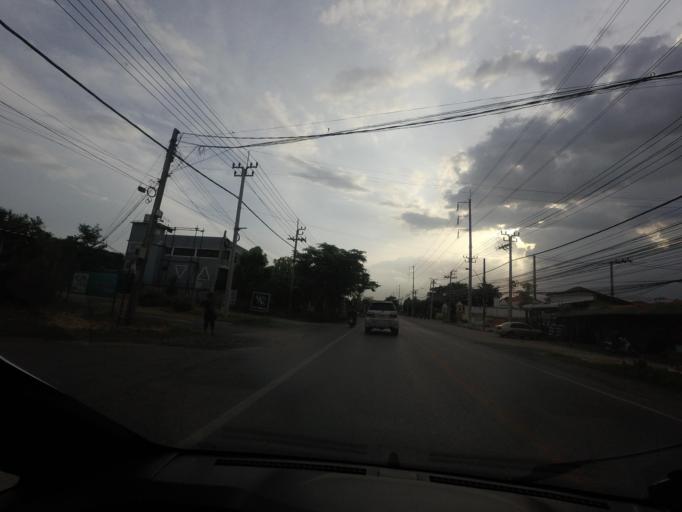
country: TH
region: Bangkok
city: Nong Chok
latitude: 13.8551
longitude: 100.8159
